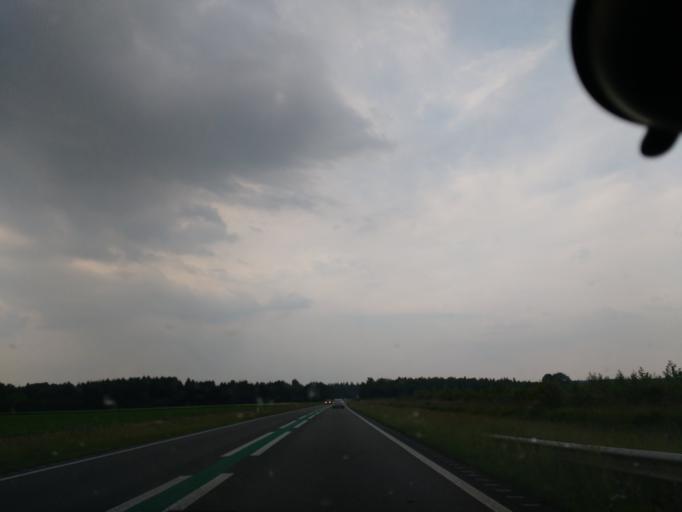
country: NL
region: Drenthe
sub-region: Gemeente Coevorden
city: Sleen
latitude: 52.8403
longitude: 6.8323
